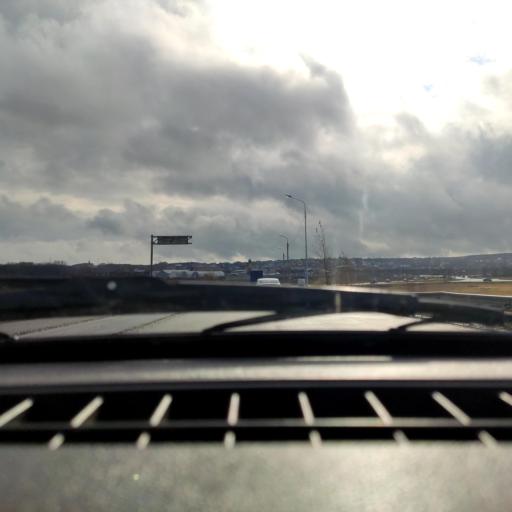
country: RU
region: Bashkortostan
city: Kabakovo
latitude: 54.6482
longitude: 56.0831
